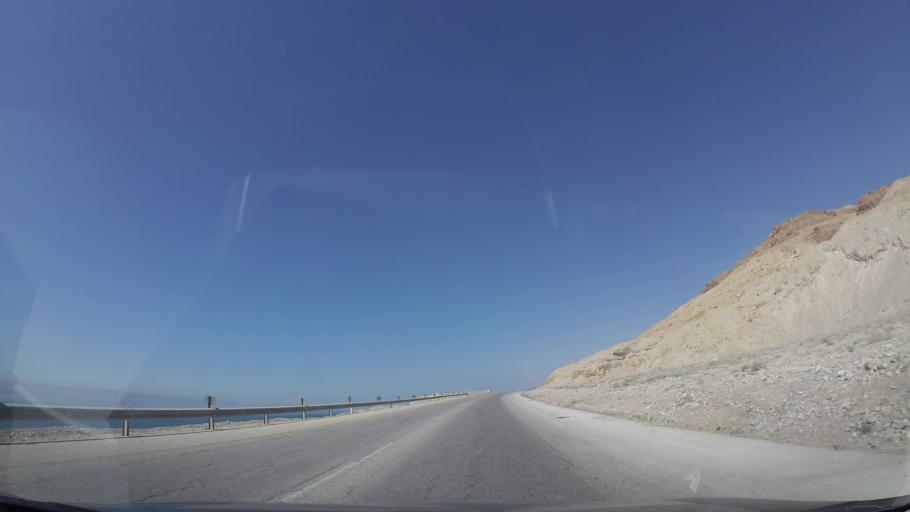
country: JO
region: Karak
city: Al Qasr
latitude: 31.3673
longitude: 35.5468
